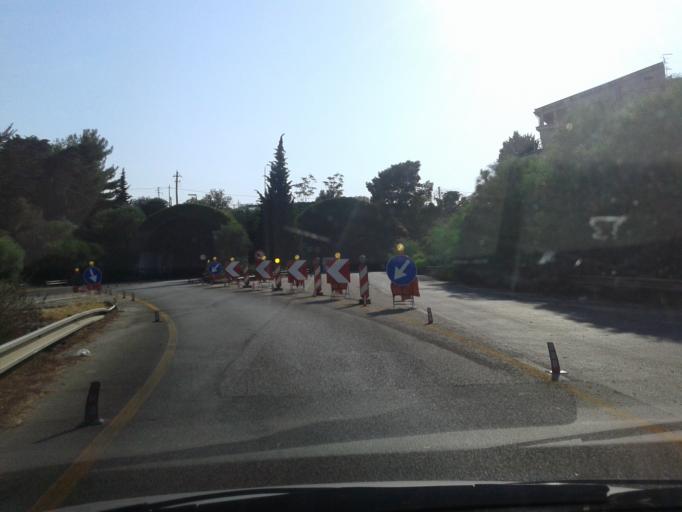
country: IT
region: Sicily
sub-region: Palermo
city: Campofelice di Roccella
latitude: 37.9857
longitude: 13.8870
